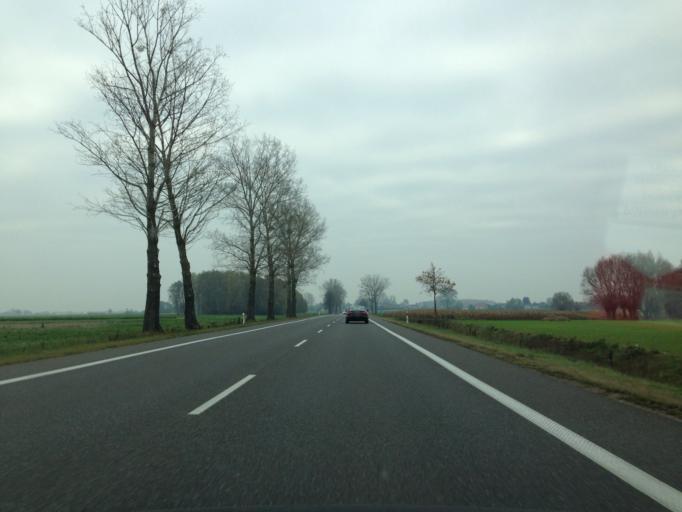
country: PL
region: Masovian Voivodeship
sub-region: Powiat plocki
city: Drobin
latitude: 52.7001
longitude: 20.0399
